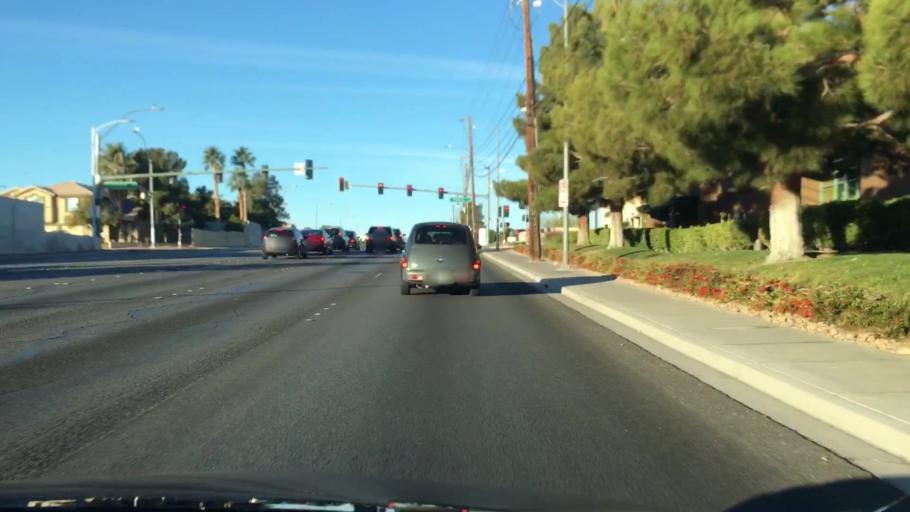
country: US
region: Nevada
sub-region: Clark County
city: Paradise
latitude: 36.0572
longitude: -115.1491
